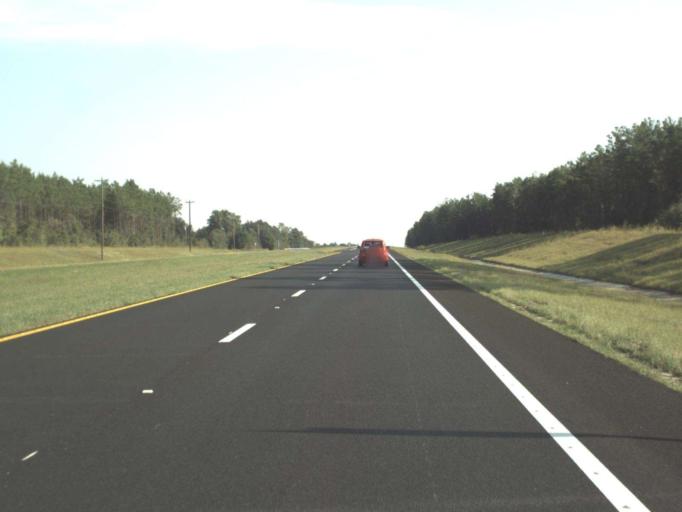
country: US
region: Florida
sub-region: Walton County
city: Freeport
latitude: 30.5315
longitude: -85.8369
